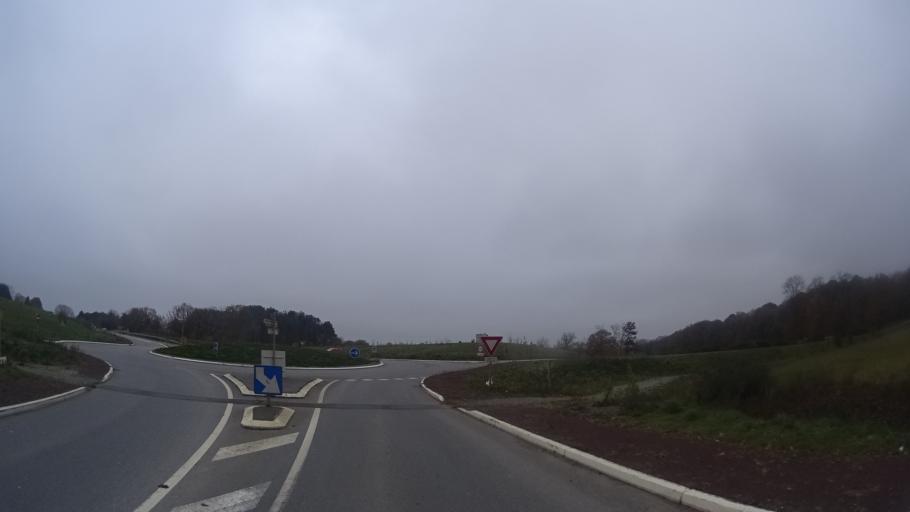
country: FR
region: Brittany
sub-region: Departement d'Ille-et-Vilaine
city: Bains-sur-Oust
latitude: 47.6912
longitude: -2.0575
